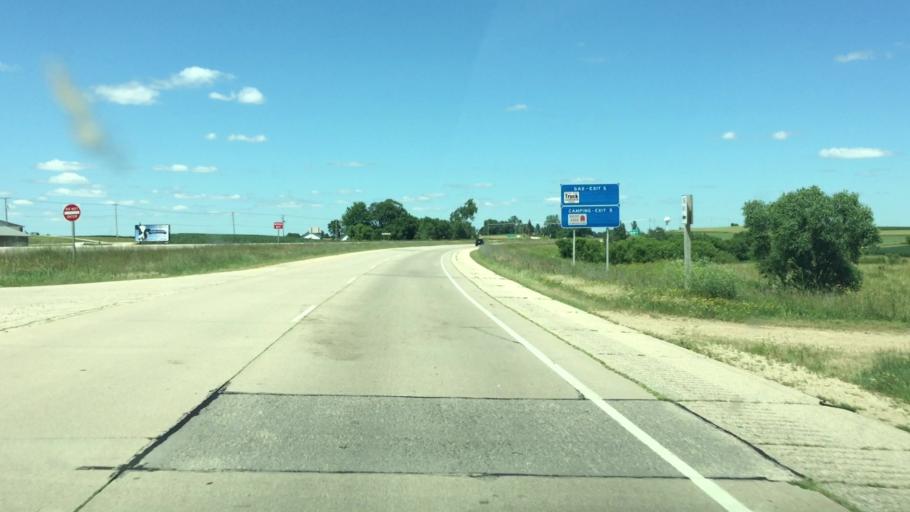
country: US
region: Wisconsin
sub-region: Grant County
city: Dickeyville
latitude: 42.5700
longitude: -90.6121
